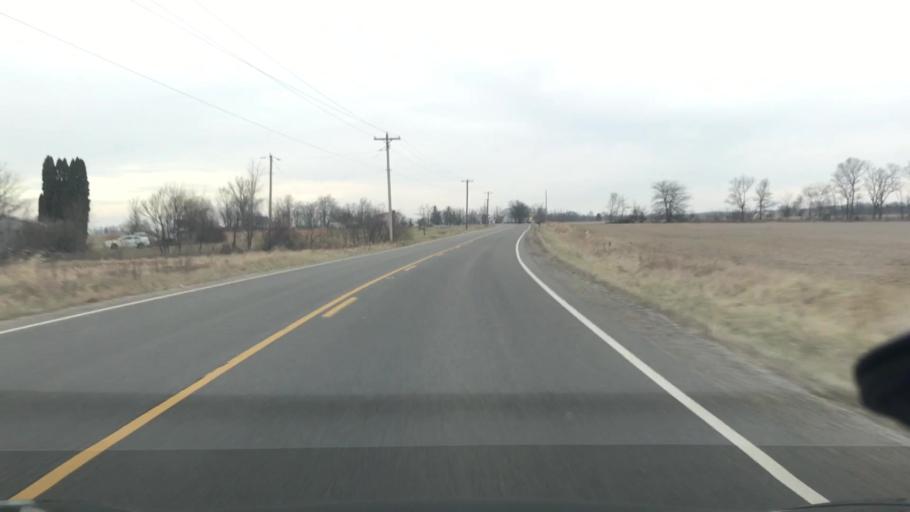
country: US
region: Ohio
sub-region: Madison County
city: Mount Sterling
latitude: 39.7732
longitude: -83.3159
